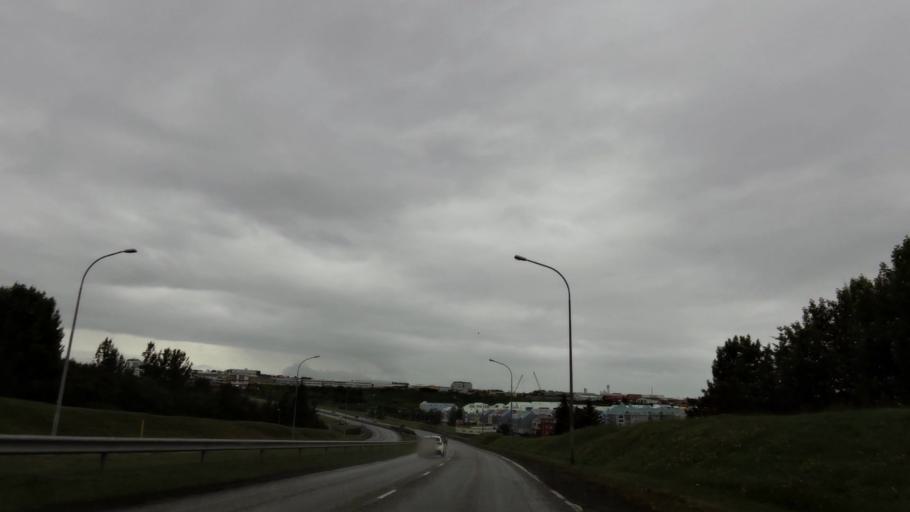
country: IS
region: Capital Region
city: Reykjavik
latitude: 64.1357
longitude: -21.8120
